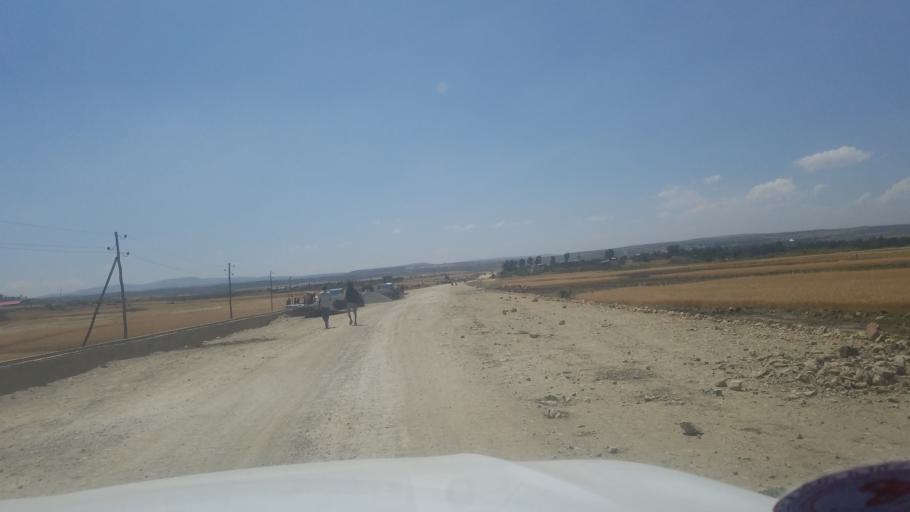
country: ET
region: Tigray
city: Mekele
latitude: 13.7682
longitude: 39.5914
